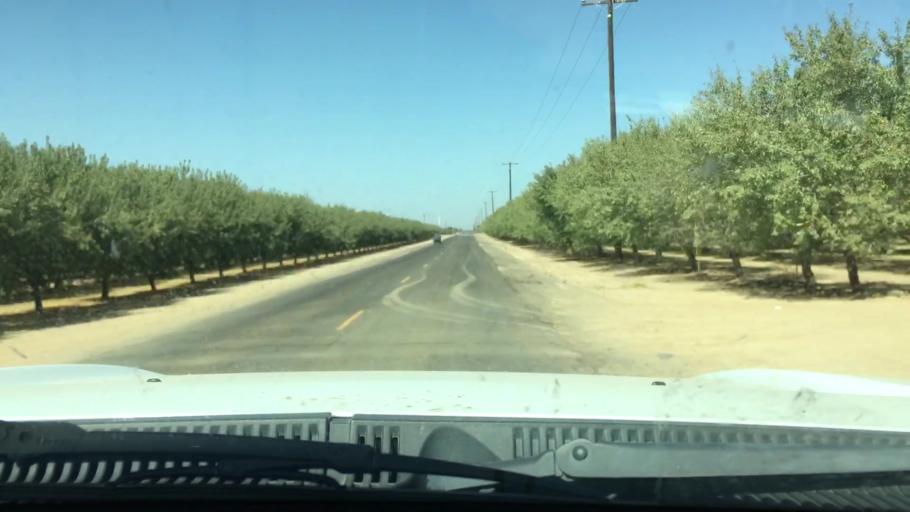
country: US
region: California
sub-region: Kern County
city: Shafter
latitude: 35.4600
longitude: -119.3143
